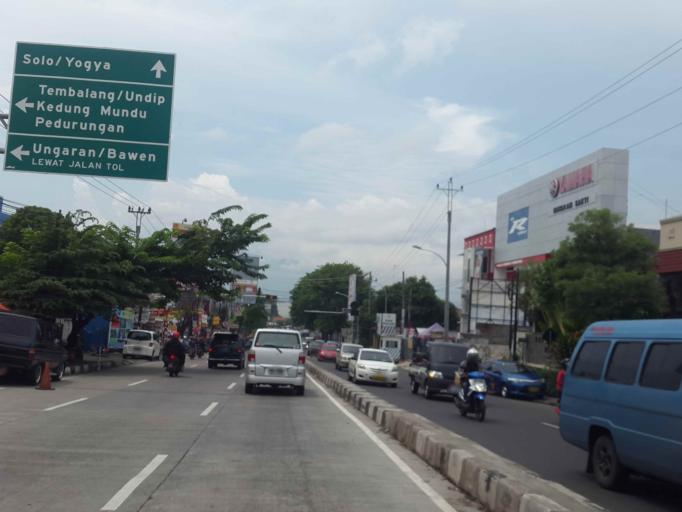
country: ID
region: Central Java
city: Semarang
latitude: -7.0477
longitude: 110.4202
